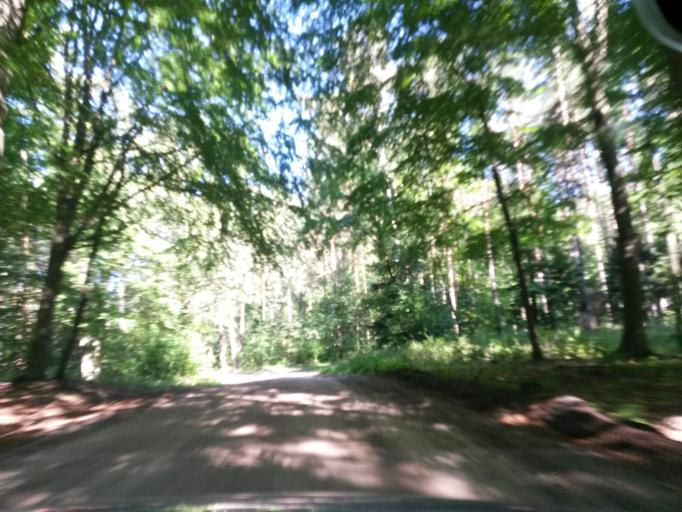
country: DE
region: Brandenburg
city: Templin
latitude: 53.2007
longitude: 13.4551
